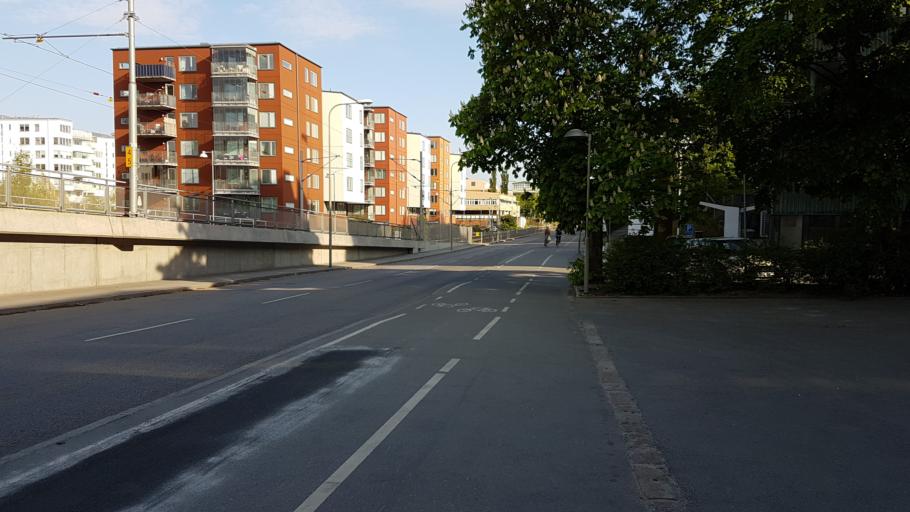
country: SE
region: Stockholm
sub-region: Sundbybergs Kommun
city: Sundbyberg
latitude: 59.3595
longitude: 17.9605
